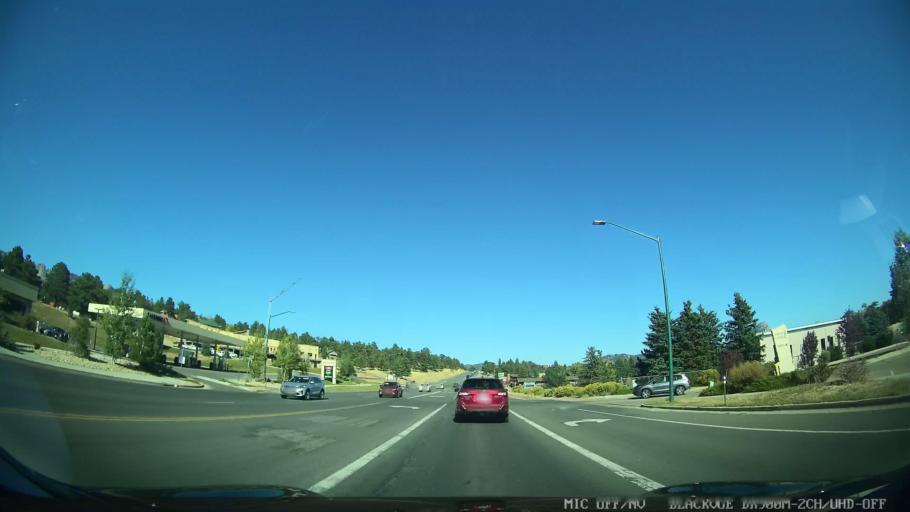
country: US
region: Colorado
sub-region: Larimer County
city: Estes Park
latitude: 40.3795
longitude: -105.5142
